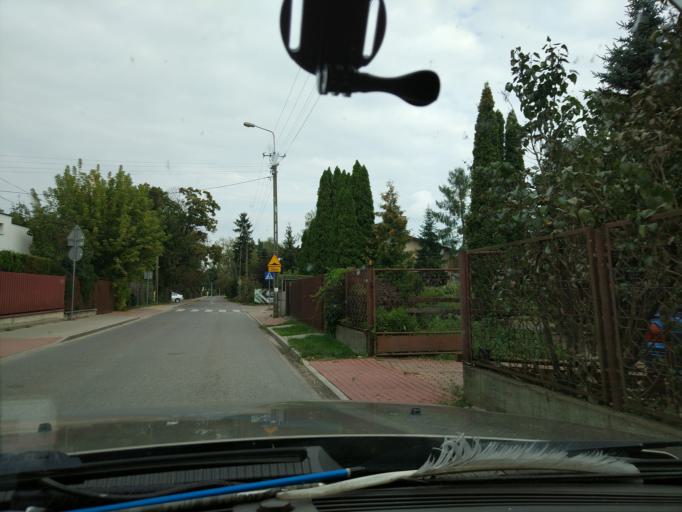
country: PL
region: Masovian Voivodeship
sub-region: Powiat pruszkowski
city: Otrebusy
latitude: 52.1282
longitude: 20.7548
